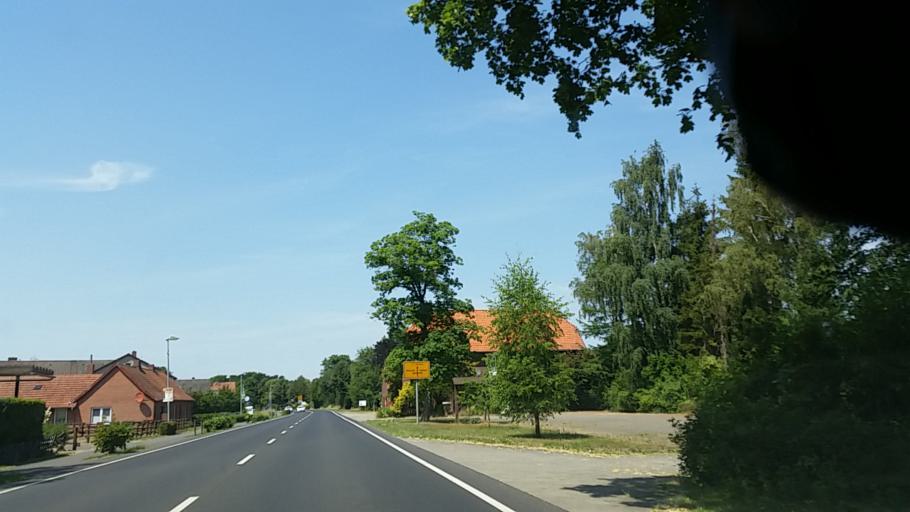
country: DE
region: Lower Saxony
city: Wietzen
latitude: 52.7081
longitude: 9.0755
